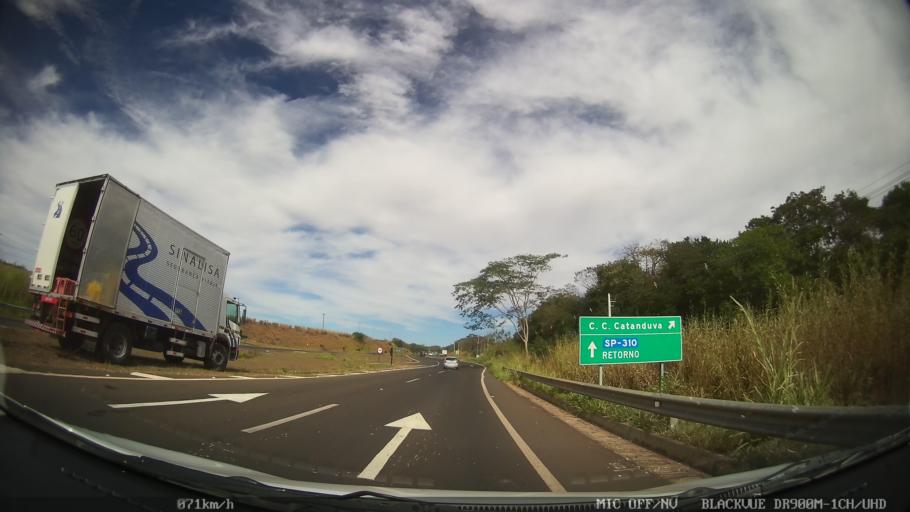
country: BR
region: Sao Paulo
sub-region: Catanduva
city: Catanduva
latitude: -21.1641
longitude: -48.9888
